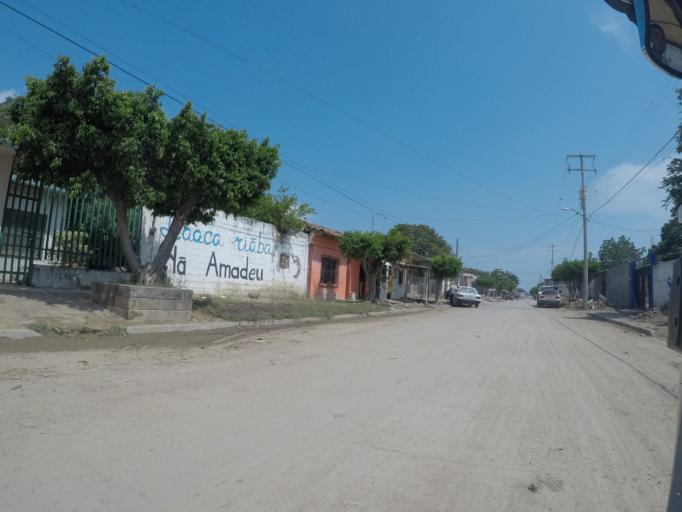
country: MX
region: Oaxaca
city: Union Hidalgo
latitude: 16.4736
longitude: -94.8354
